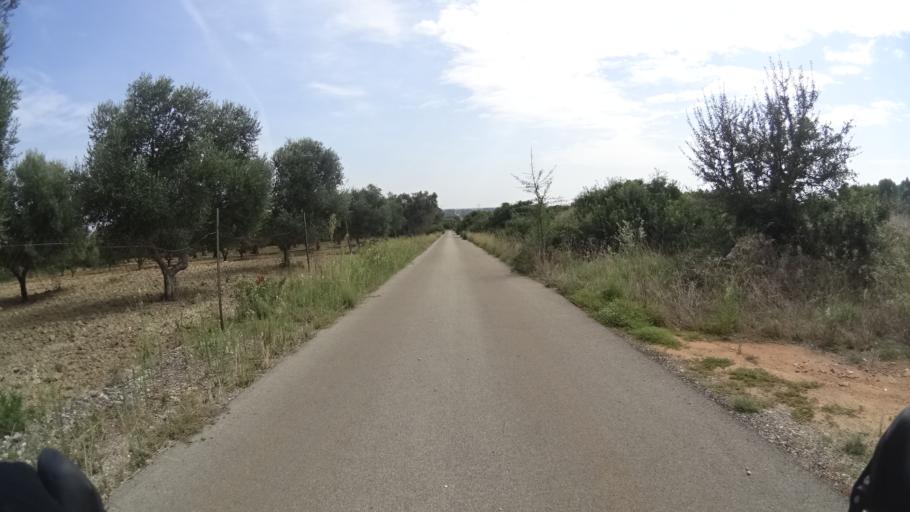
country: IT
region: Apulia
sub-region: Provincia di Lecce
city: Porto Cesareo
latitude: 40.2985
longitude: 17.9168
